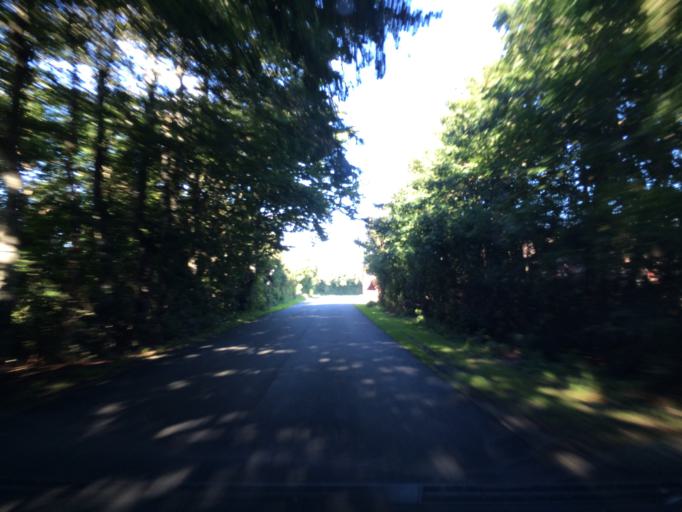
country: DK
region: Central Jutland
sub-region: Holstebro Kommune
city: Holstebro
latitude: 56.3232
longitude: 8.6750
